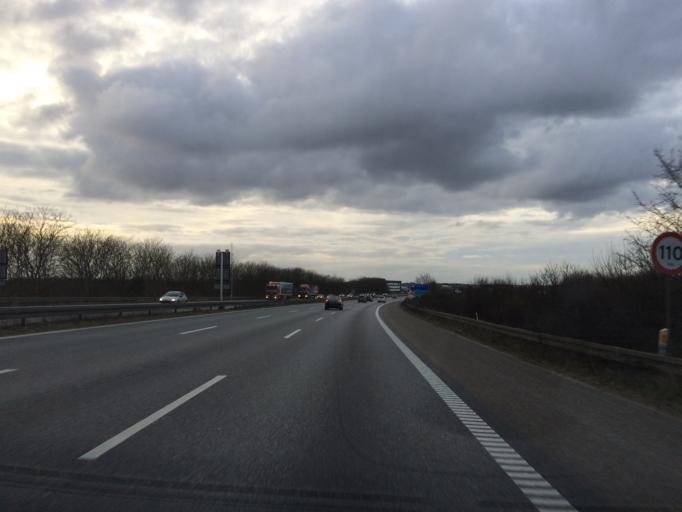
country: DK
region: South Denmark
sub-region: Fredericia Kommune
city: Snoghoj
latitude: 55.5219
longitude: 9.7345
